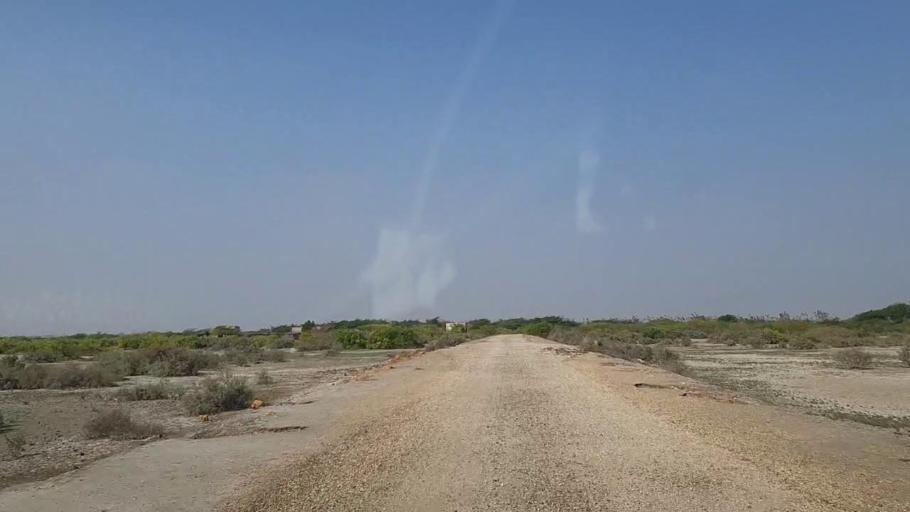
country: PK
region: Sindh
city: Mirpur Sakro
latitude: 24.6599
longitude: 67.7264
